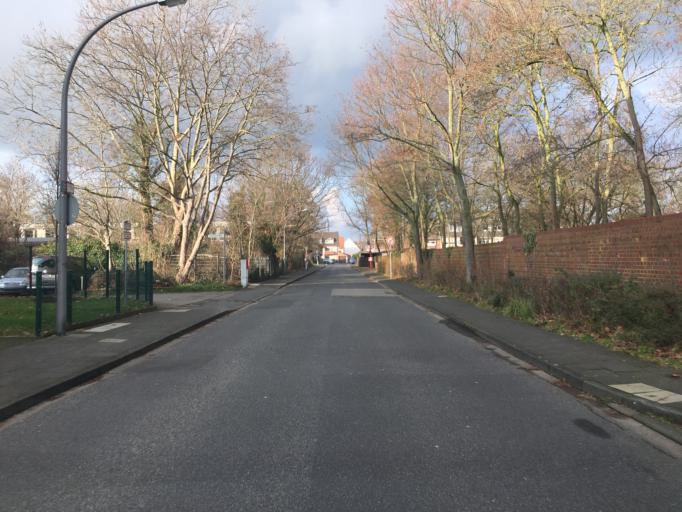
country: DE
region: North Rhine-Westphalia
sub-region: Regierungsbezirk Dusseldorf
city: Dormagen
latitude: 51.0607
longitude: 6.8570
